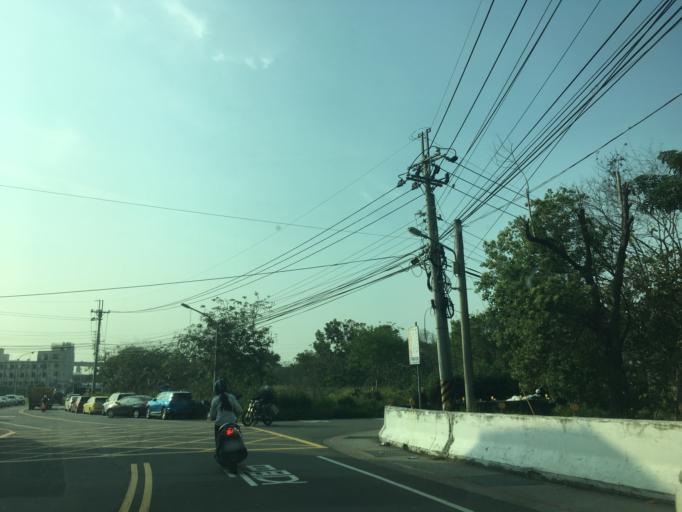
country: TW
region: Taiwan
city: Zhongxing New Village
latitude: 24.0497
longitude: 120.6865
